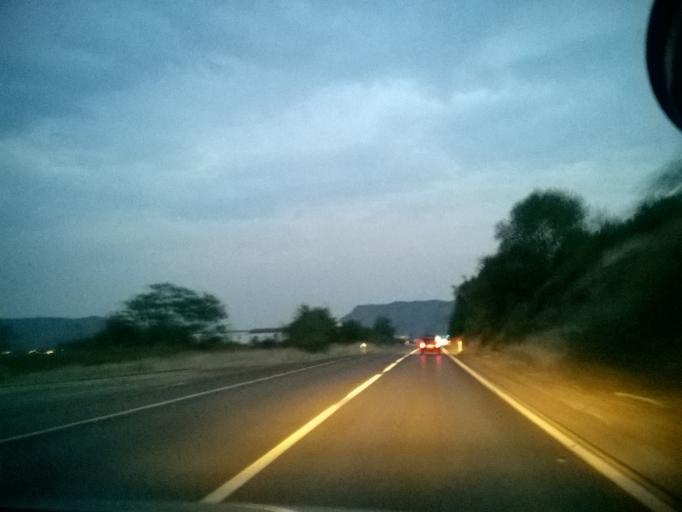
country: ME
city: Spuz
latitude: 42.4777
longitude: 19.1702
